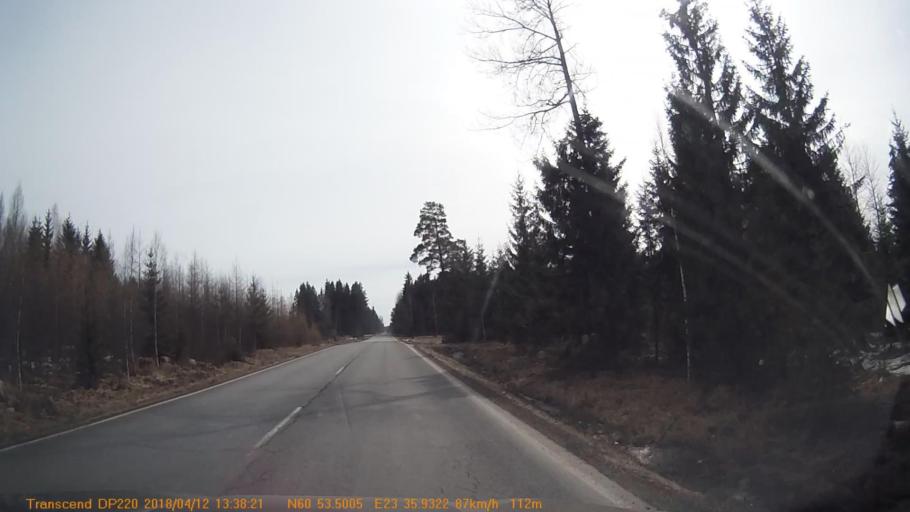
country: FI
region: Haeme
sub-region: Forssa
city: Forssa
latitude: 60.8915
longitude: 23.5990
